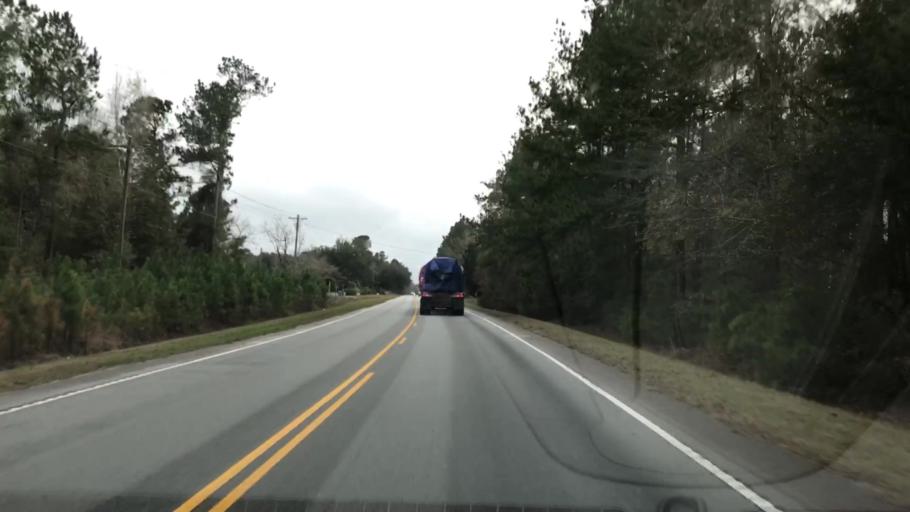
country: US
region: South Carolina
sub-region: Berkeley County
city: Bonneau Beach
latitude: 33.2536
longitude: -79.9367
